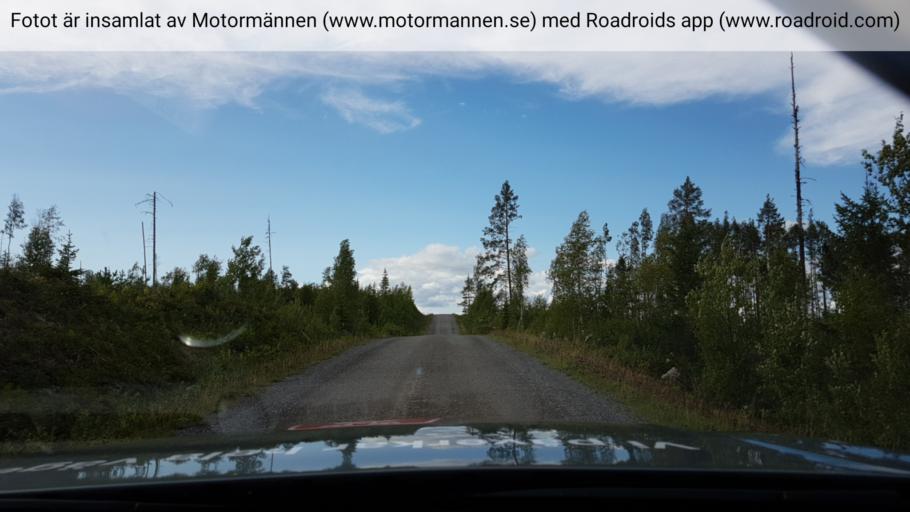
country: SE
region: Jaemtland
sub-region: OEstersunds Kommun
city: Lit
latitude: 63.2930
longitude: 15.3422
